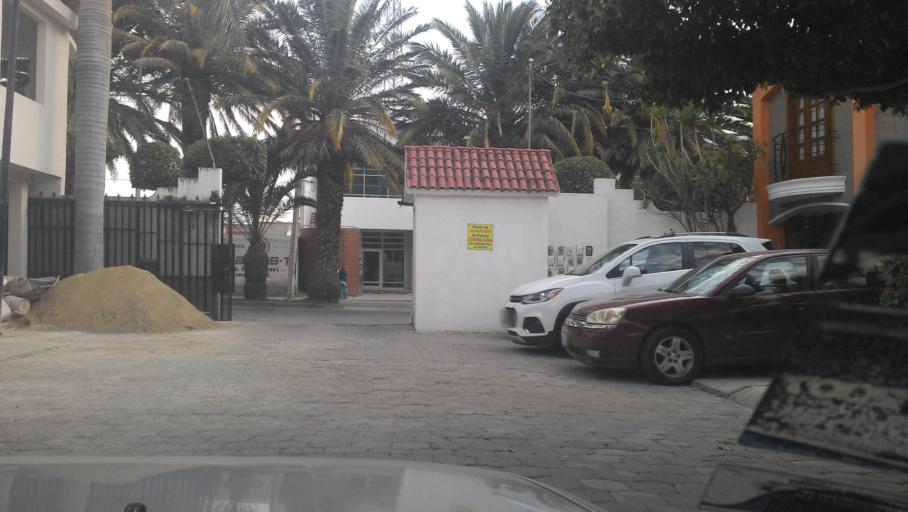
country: MX
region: Guanajuato
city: San Francisco del Rincon
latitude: 21.0141
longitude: -101.8604
